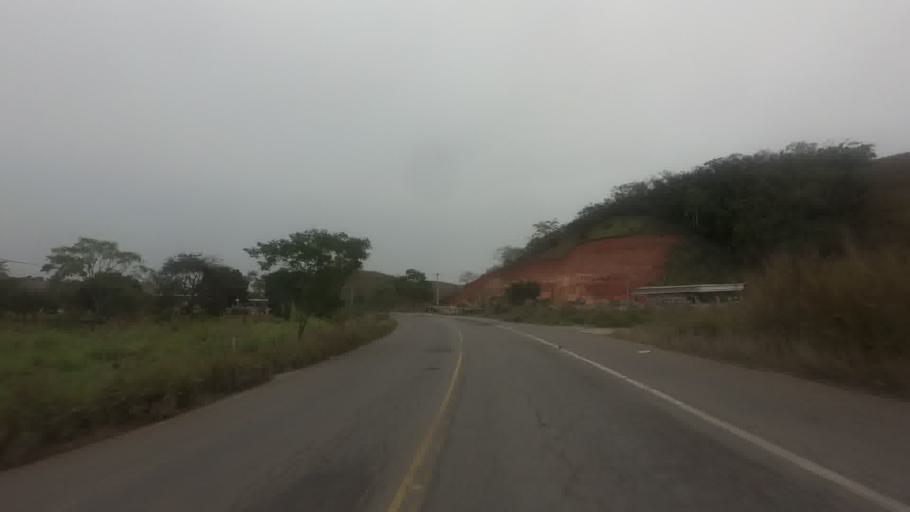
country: BR
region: Rio de Janeiro
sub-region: Santo Antonio De Padua
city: Santo Antonio de Padua
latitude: -21.6557
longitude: -42.3247
